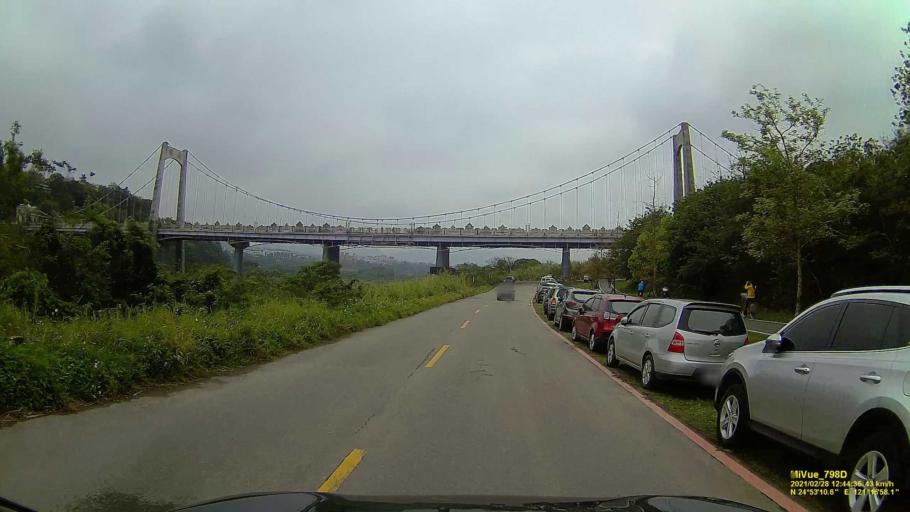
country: TW
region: Taiwan
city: Daxi
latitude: 24.8862
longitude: 121.2828
